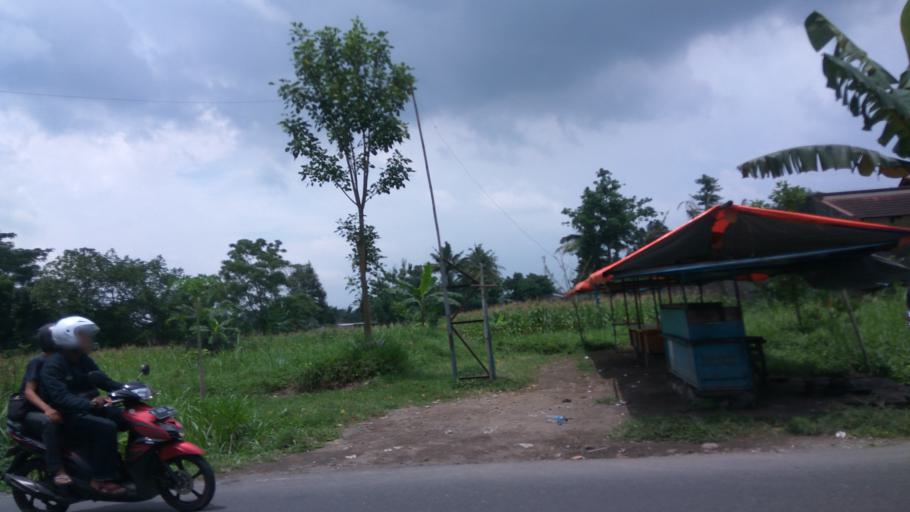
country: ID
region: Daerah Istimewa Yogyakarta
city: Melati
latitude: -7.7256
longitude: 110.4005
